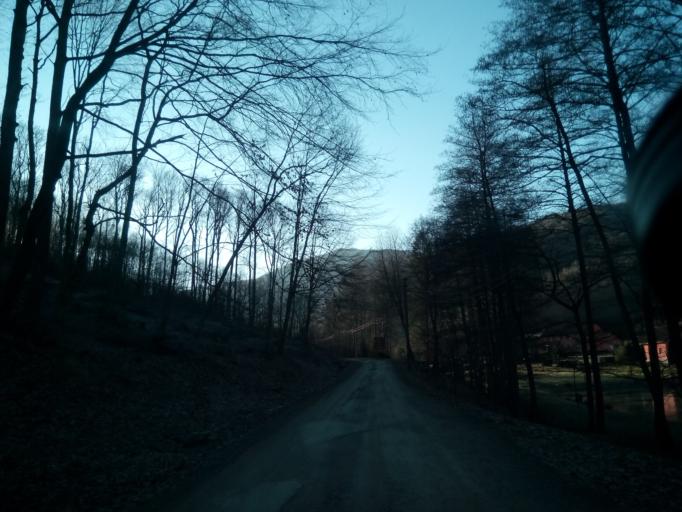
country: SK
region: Kosicky
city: Medzev
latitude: 48.6793
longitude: 20.8839
